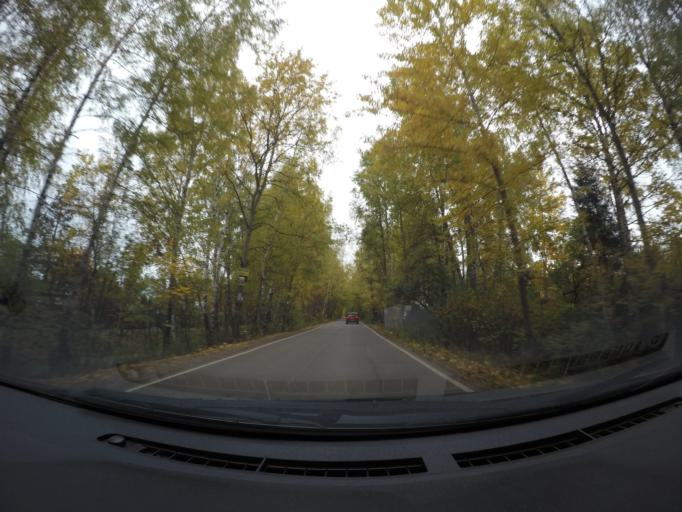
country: RU
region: Moskovskaya
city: Imeni Vorovskogo
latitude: 55.7318
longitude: 38.3015
